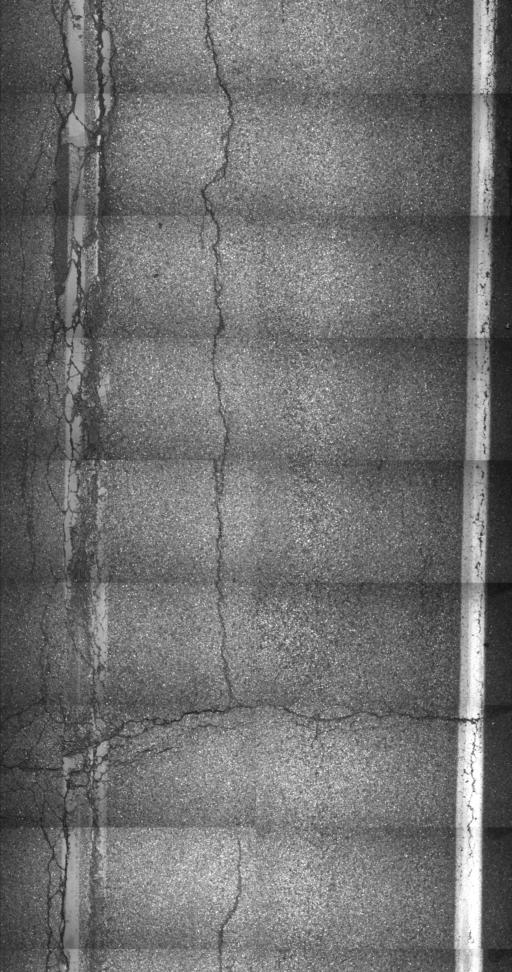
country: US
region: Massachusetts
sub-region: Franklin County
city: Charlemont
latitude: 42.7680
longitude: -72.9311
